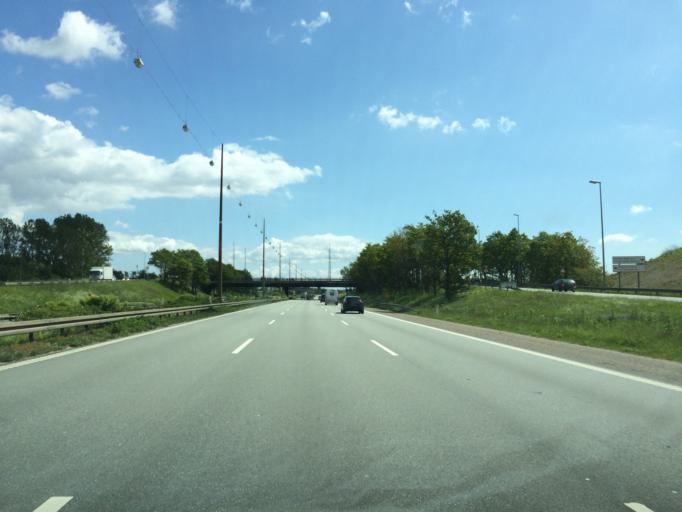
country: DK
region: Capital Region
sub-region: Vallensbaek Kommune
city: Vallensbaek
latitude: 55.6424
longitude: 12.3685
